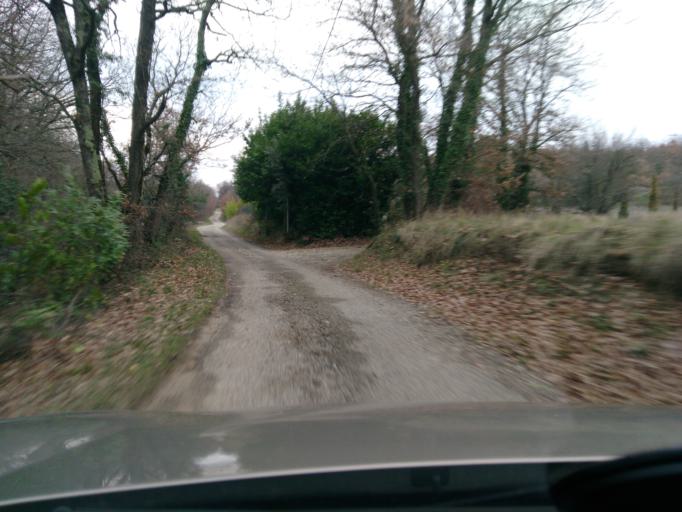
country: FR
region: Rhone-Alpes
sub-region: Departement de la Drome
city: Montboucher-sur-Jabron
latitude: 44.5305
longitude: 4.8258
